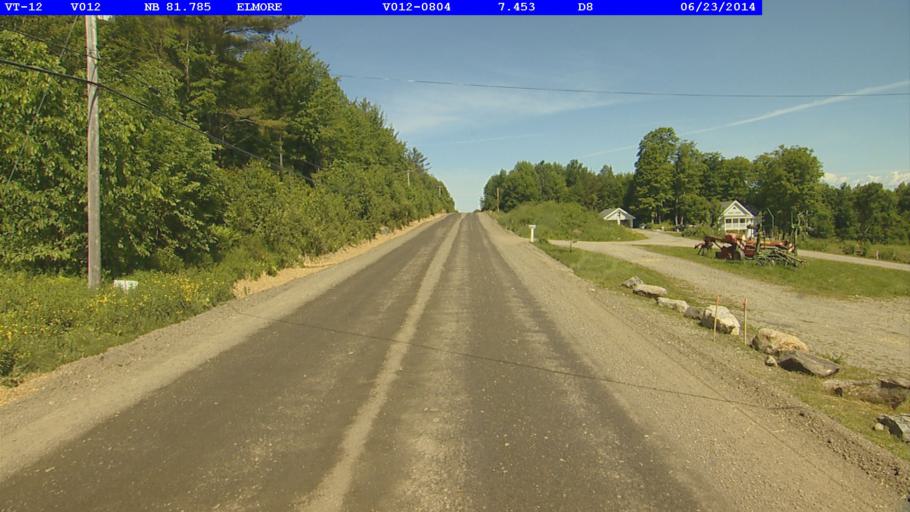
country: US
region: Vermont
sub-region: Lamoille County
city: Morrisville
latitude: 44.5482
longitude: -72.5330
